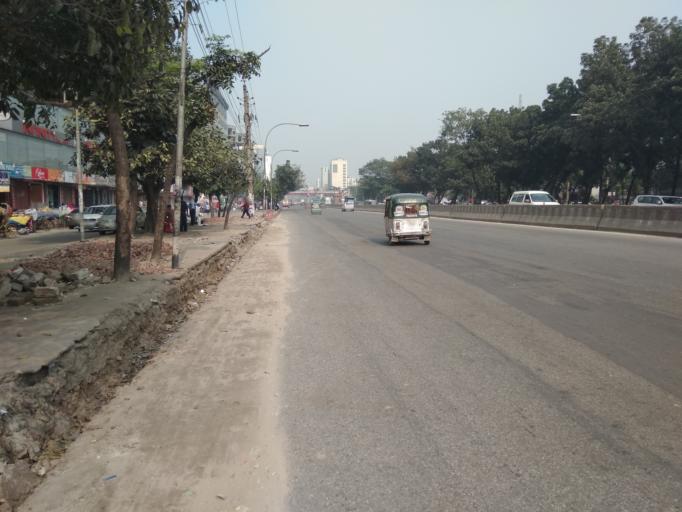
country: BD
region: Dhaka
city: Tungi
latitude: 23.8661
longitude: 90.4001
